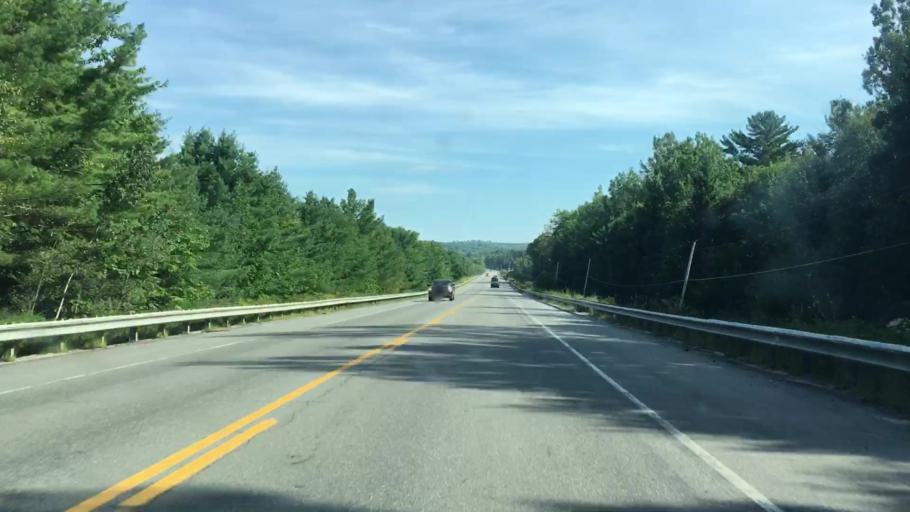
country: US
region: Maine
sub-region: Penobscot County
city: Lincoln
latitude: 45.3671
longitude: -68.5528
